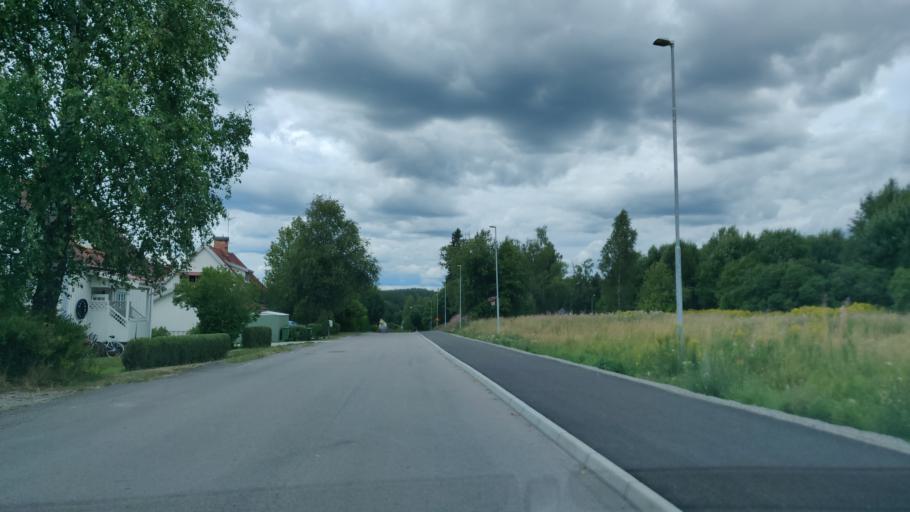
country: SE
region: Vaermland
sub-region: Hagfors Kommun
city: Hagfors
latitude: 60.0404
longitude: 13.6847
